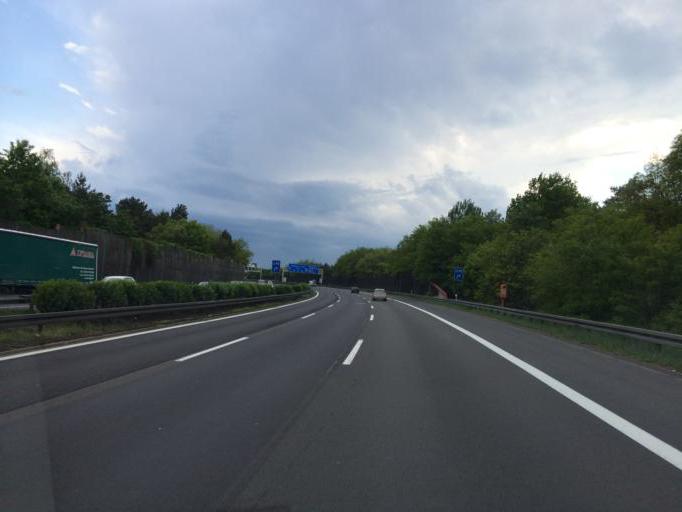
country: DE
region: Brandenburg
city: Michendorf
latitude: 52.3013
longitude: 13.0475
